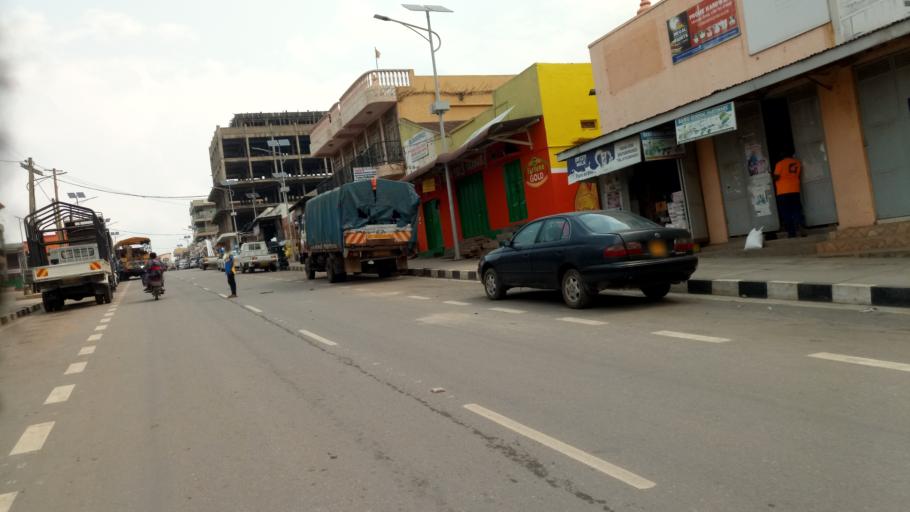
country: UG
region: Western Region
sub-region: Mbarara District
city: Mbarara
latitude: -0.6047
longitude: 30.6635
